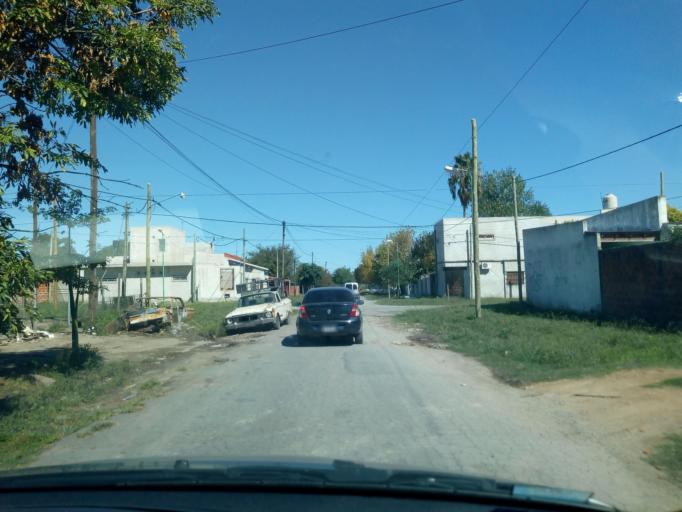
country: AR
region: Buenos Aires
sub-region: Partido de La Plata
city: La Plata
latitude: -35.0003
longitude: -58.0455
